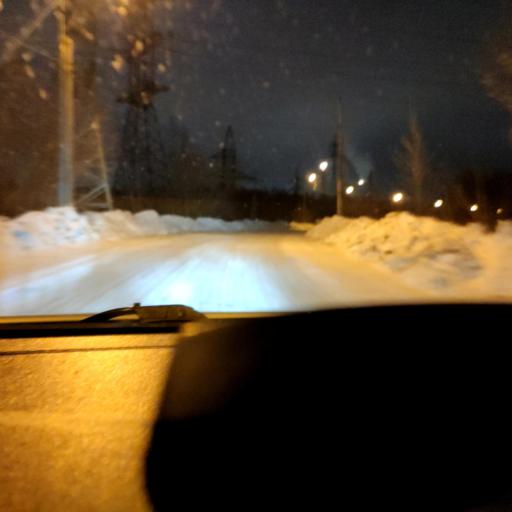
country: RU
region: Tatarstan
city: Staroye Arakchino
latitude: 55.8739
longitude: 48.9586
